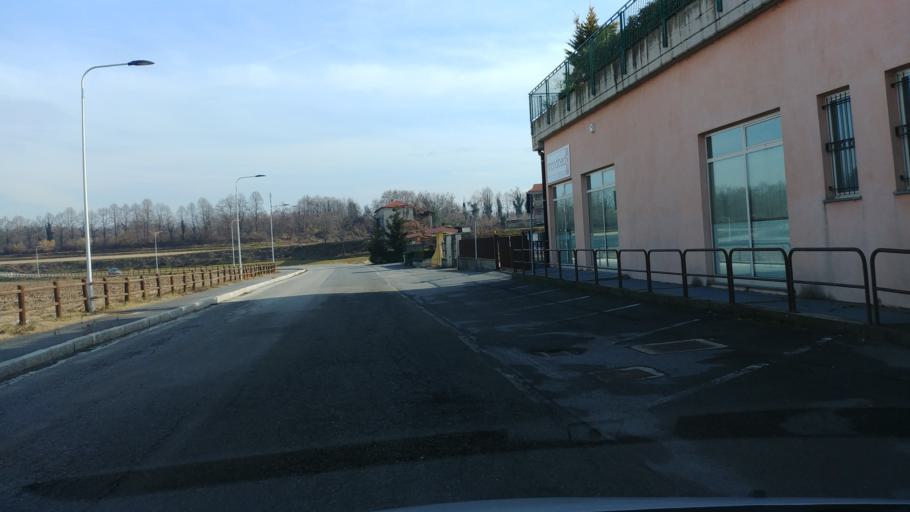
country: IT
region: Piedmont
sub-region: Provincia di Cuneo
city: Cuneo
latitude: 44.3932
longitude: 7.5657
